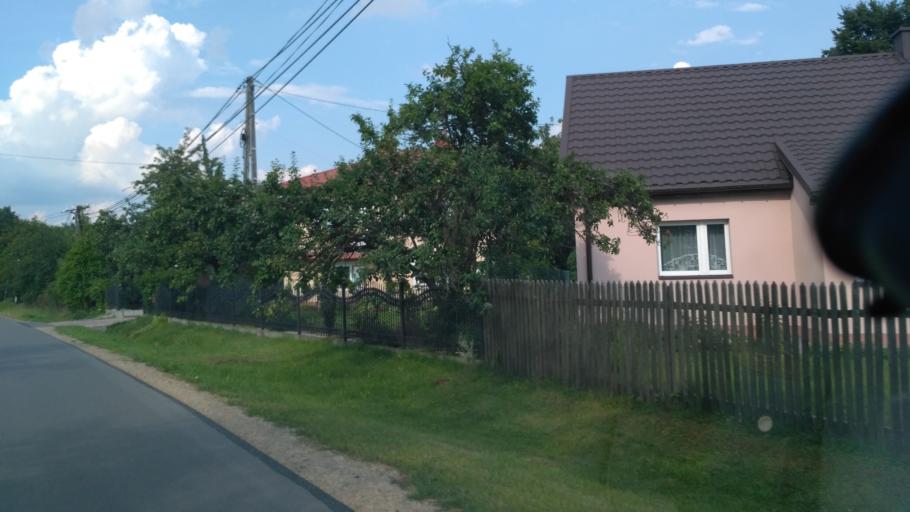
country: PL
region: Subcarpathian Voivodeship
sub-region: Powiat rzeszowski
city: Glogow Malopolski
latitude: 50.1571
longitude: 21.9807
